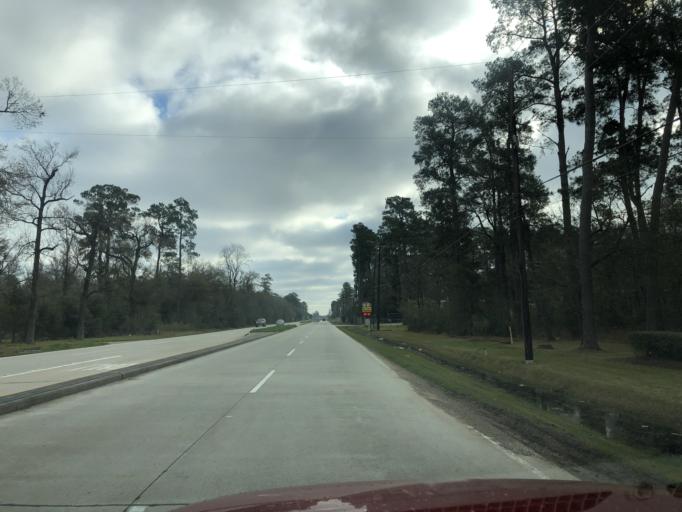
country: US
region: Texas
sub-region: Harris County
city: Spring
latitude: 30.0828
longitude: -95.4609
